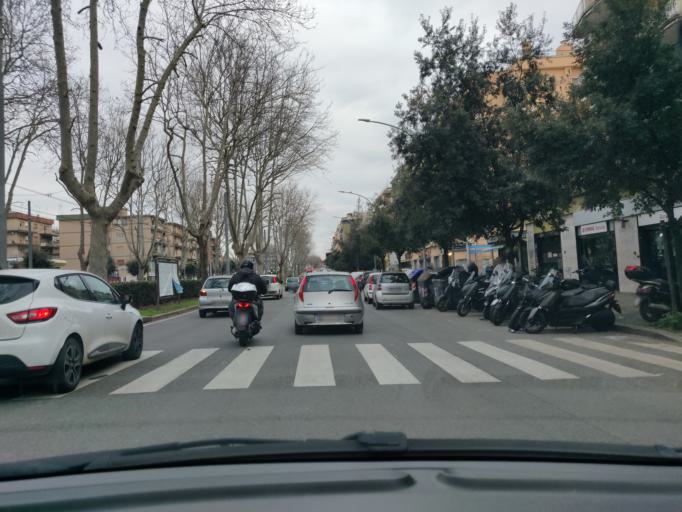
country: VA
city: Vatican City
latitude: 41.8766
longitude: 12.4438
